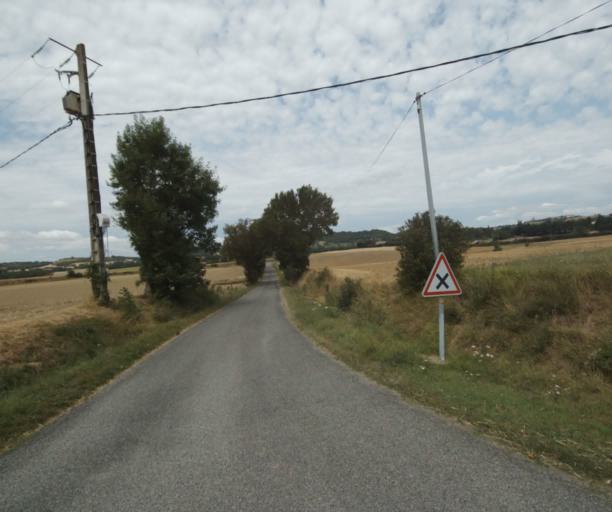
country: FR
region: Midi-Pyrenees
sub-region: Departement de la Haute-Garonne
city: Saint-Felix-Lauragais
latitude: 43.4207
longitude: 1.9025
